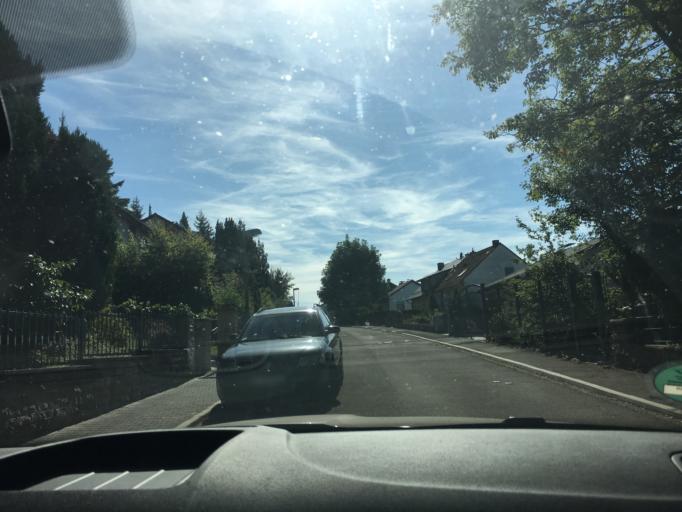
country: DE
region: Rheinland-Pfalz
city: Schopp
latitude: 49.3521
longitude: 7.6924
